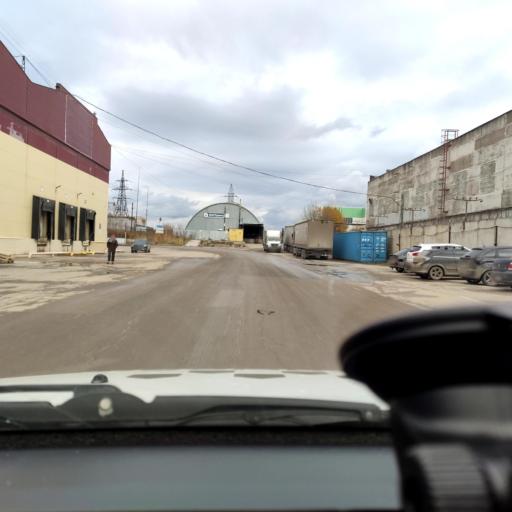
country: RU
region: Perm
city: Froly
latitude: 57.9591
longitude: 56.2779
